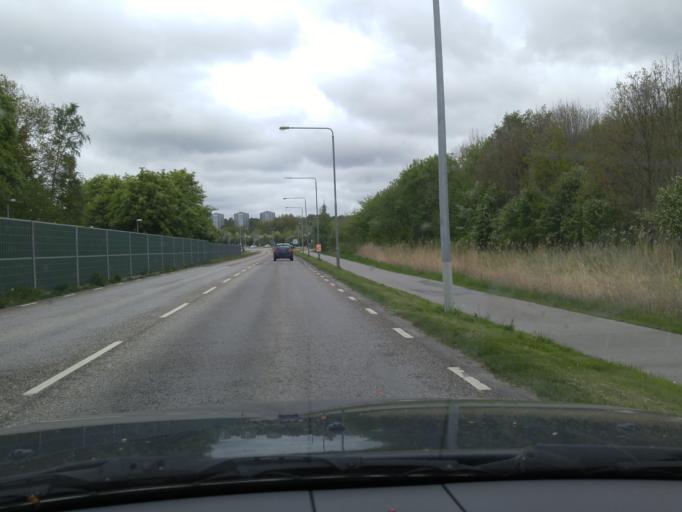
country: SE
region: Vaestra Goetaland
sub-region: Goteborg
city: Majorna
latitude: 57.6413
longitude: 11.9157
